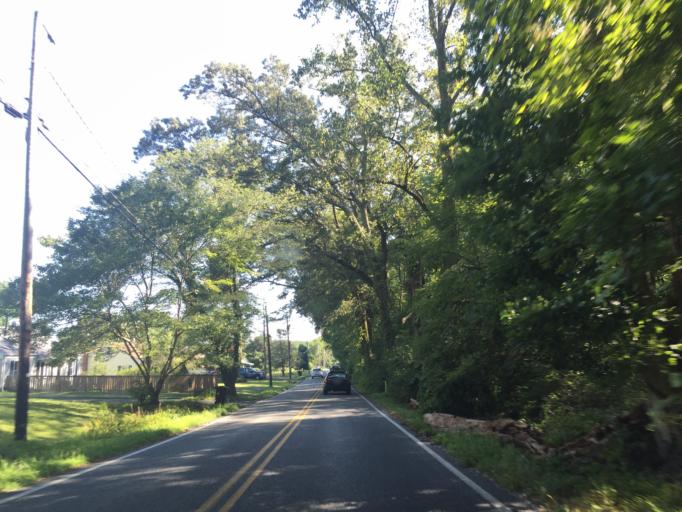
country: US
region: Maryland
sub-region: Harford County
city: Pleasant Hills
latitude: 39.4729
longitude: -76.3806
